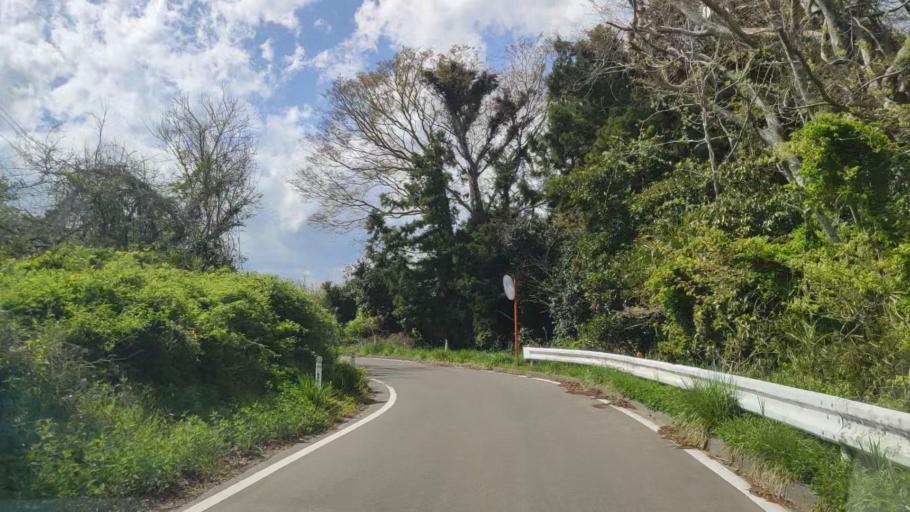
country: JP
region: Miyagi
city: Matsushima
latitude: 38.3361
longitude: 141.1471
